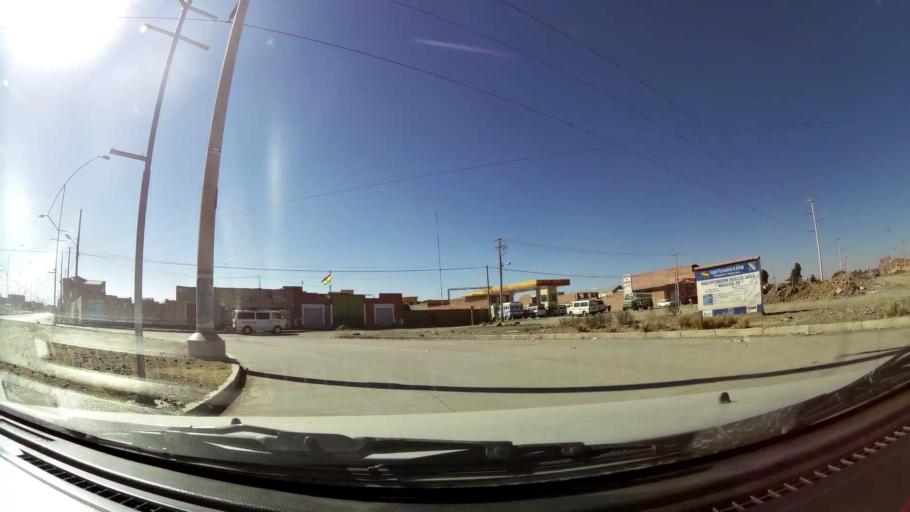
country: BO
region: La Paz
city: La Paz
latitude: -16.5346
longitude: -68.2280
